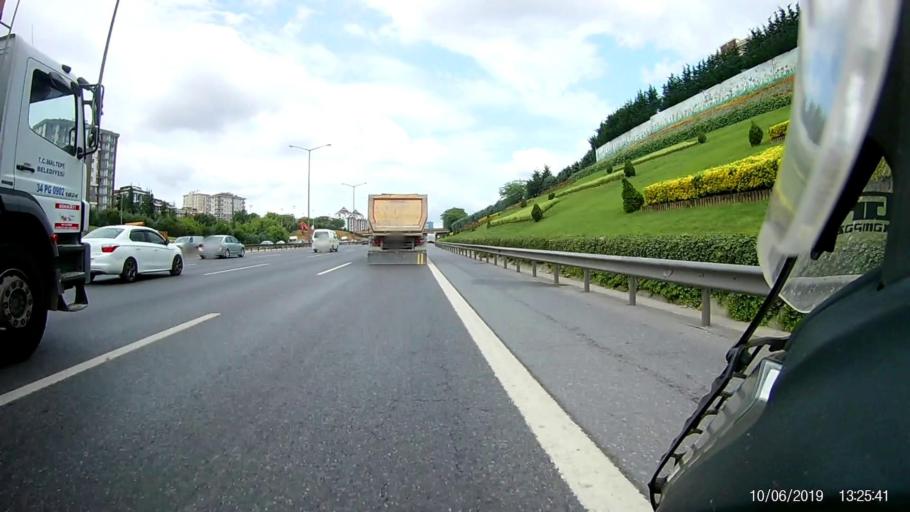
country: TR
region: Istanbul
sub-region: Atasehir
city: Atasehir
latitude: 40.9502
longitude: 29.1063
